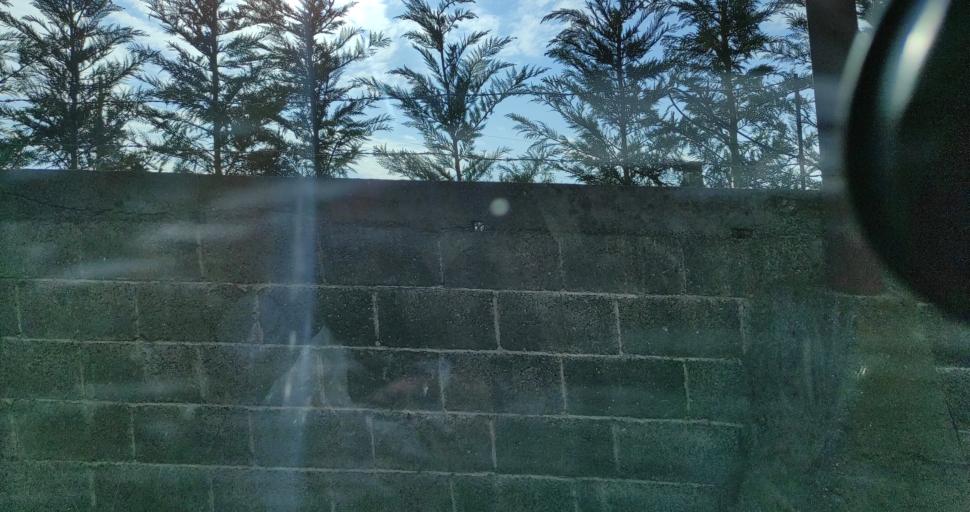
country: AL
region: Lezhe
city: Lezhe
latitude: 41.7885
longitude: 19.6267
